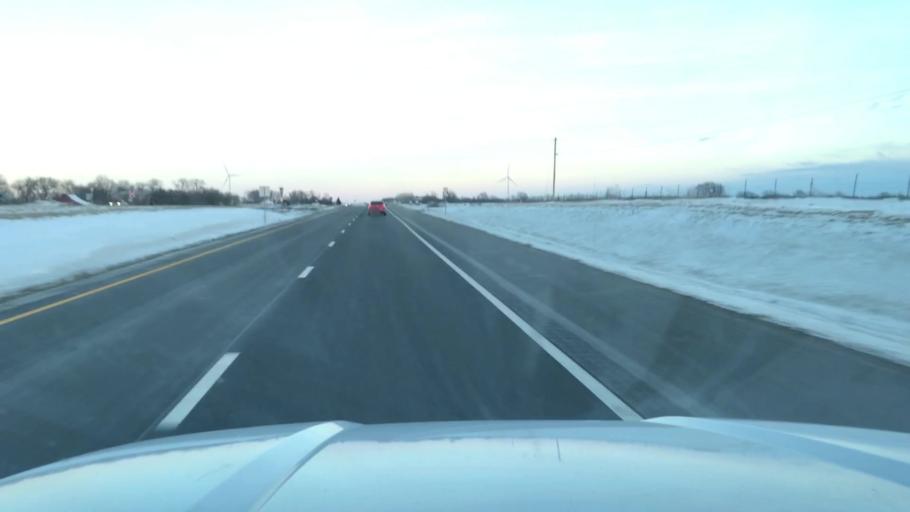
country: US
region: Missouri
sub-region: DeKalb County
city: Maysville
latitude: 39.7615
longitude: -94.4073
